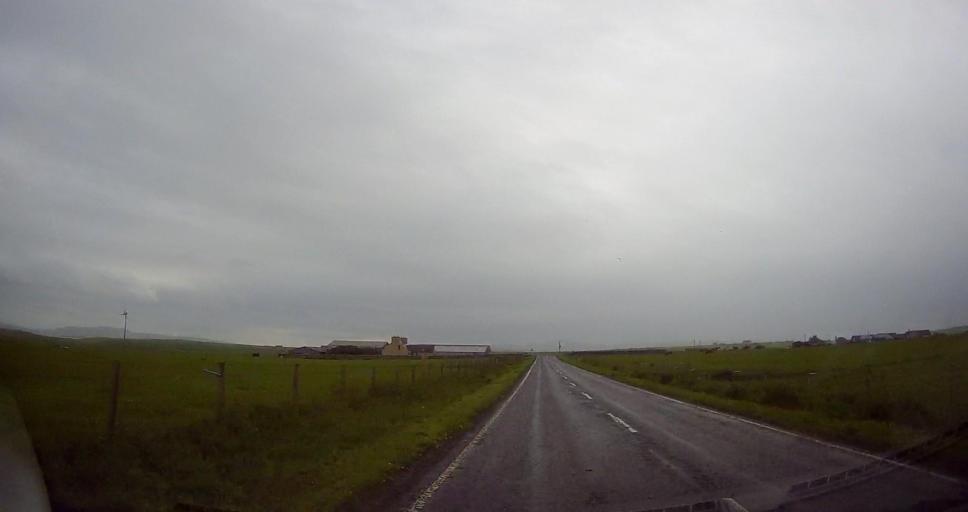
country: GB
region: Scotland
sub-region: Orkney Islands
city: Stromness
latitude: 59.0622
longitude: -3.2821
